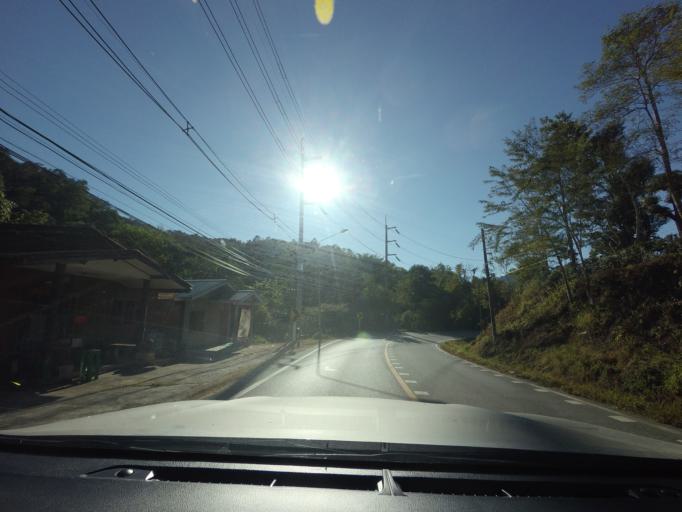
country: TH
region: Mae Hong Son
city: Mae Hi
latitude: 19.2040
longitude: 98.6727
